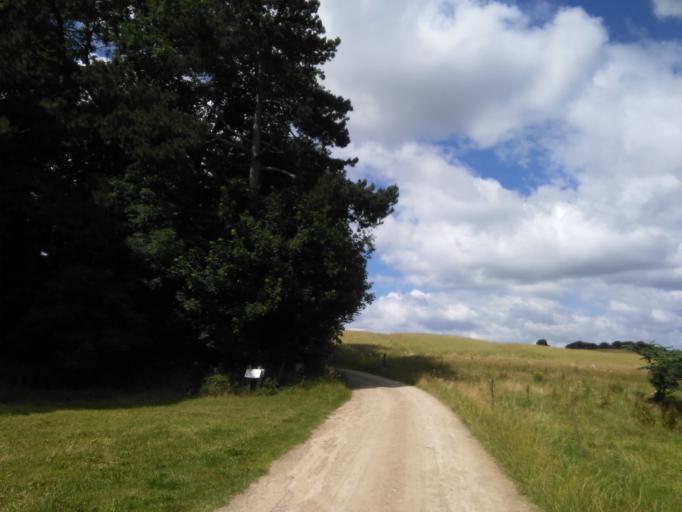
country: DK
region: Central Jutland
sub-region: Arhus Kommune
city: Logten
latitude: 56.1687
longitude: 10.4095
